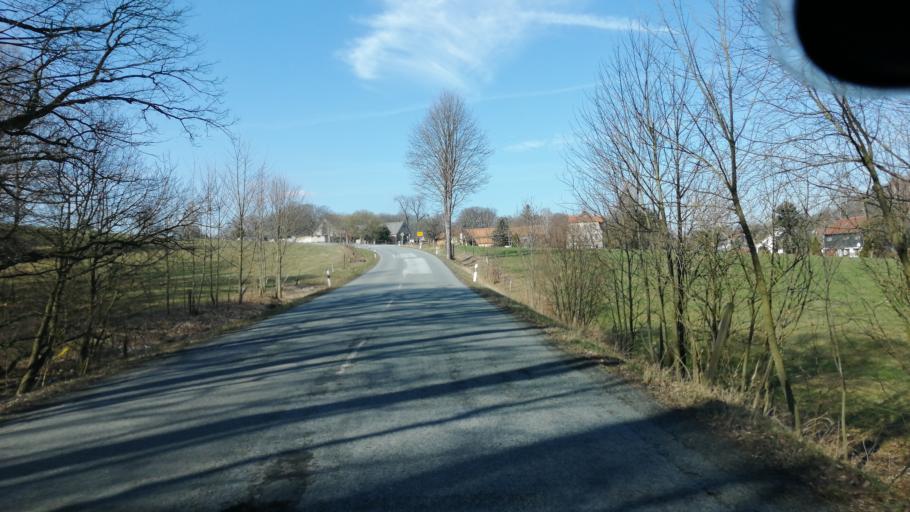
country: DE
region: Saxony
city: Schonbach
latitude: 51.0576
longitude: 14.5860
